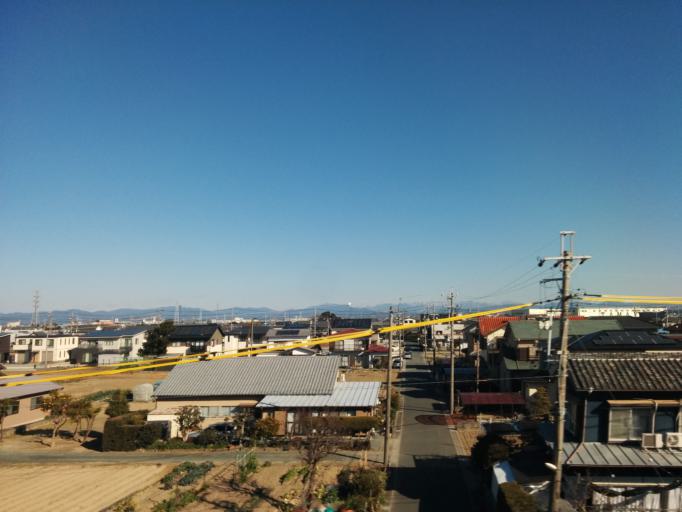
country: JP
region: Shizuoka
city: Hamamatsu
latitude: 34.7085
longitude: 137.7868
